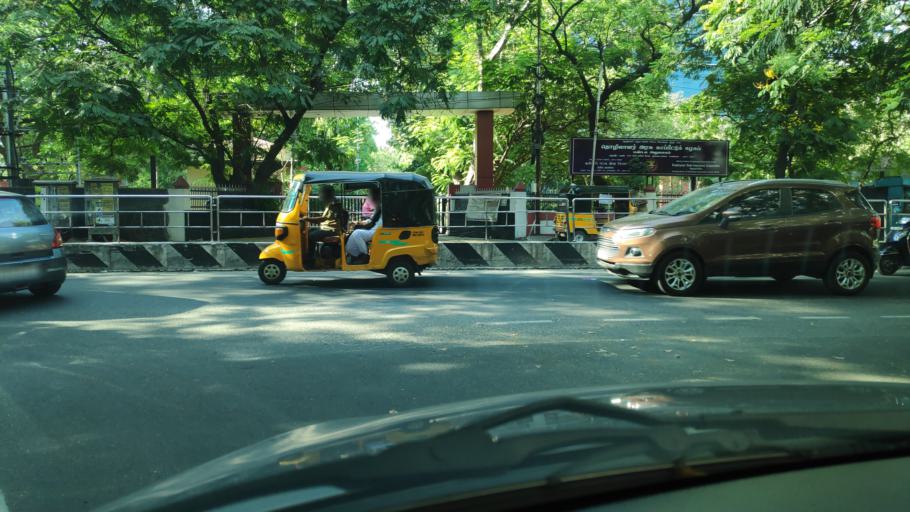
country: IN
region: Tamil Nadu
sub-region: Chennai
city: Chetput
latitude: 13.0654
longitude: 80.2415
